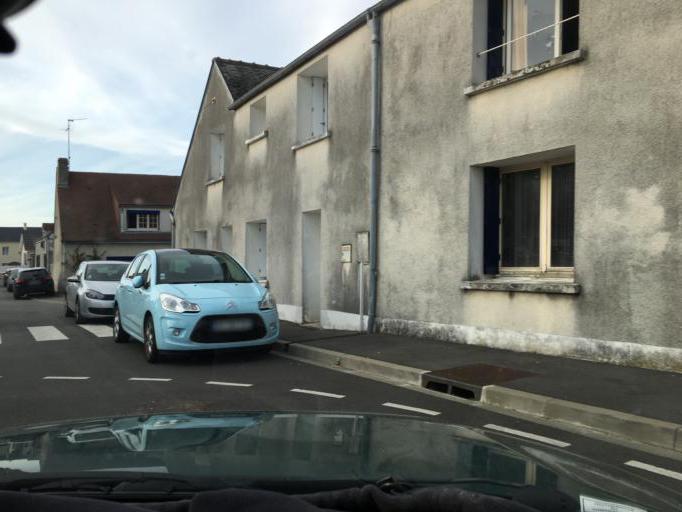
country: FR
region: Centre
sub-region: Departement du Loiret
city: Baule
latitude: 47.8120
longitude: 1.6679
